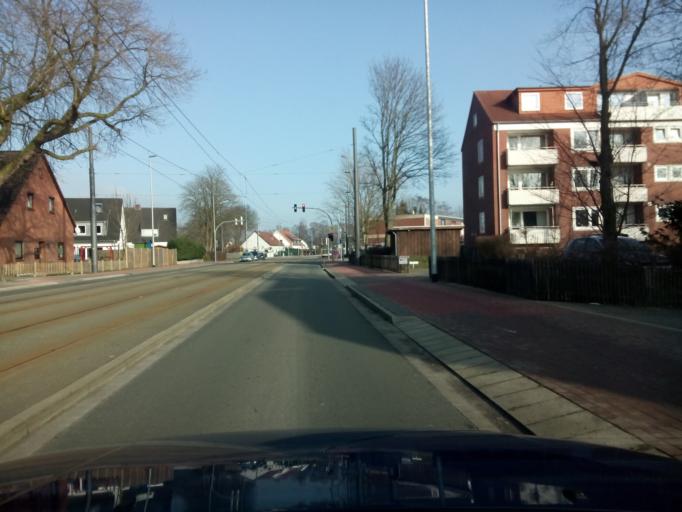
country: DE
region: Lower Saxony
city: Lilienthal
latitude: 53.1531
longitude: 8.9197
